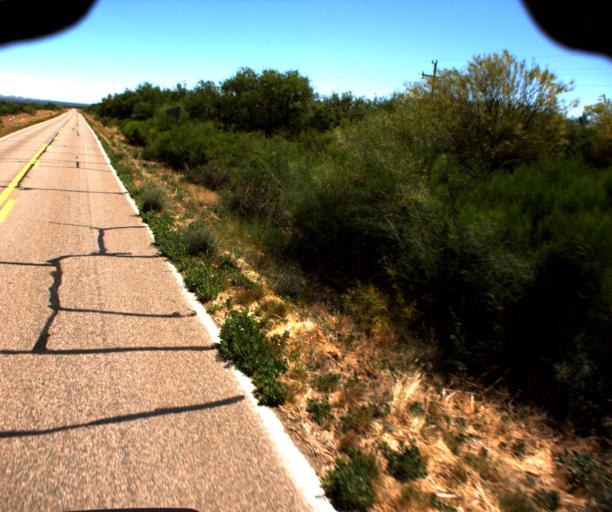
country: US
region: Arizona
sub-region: Pima County
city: Three Points
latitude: 31.7040
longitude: -111.4876
